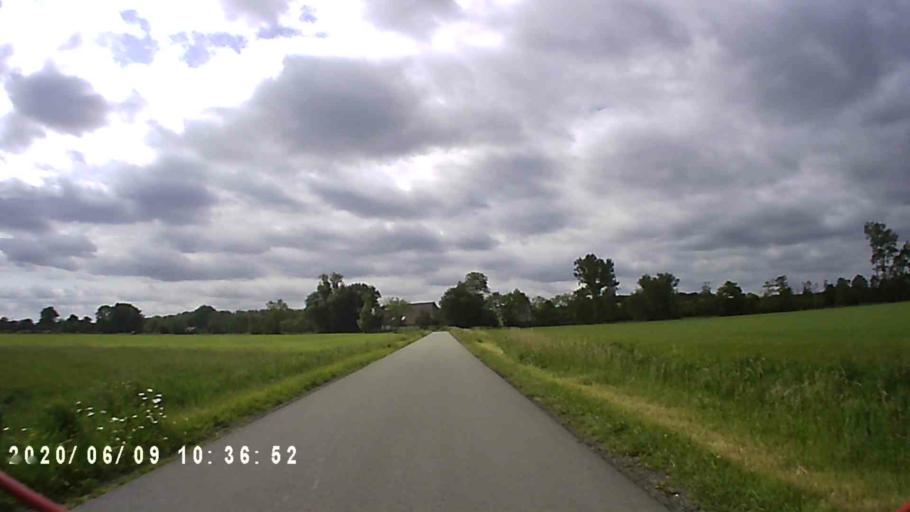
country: NL
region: Groningen
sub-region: Gemeente Groningen
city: Korrewegwijk
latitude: 53.2550
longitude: 6.5250
